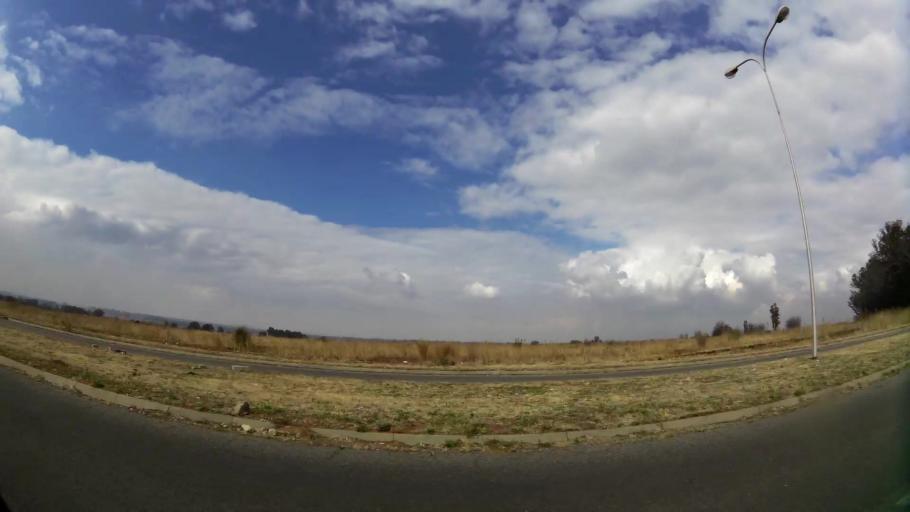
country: ZA
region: Gauteng
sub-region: Sedibeng District Municipality
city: Vanderbijlpark
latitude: -26.7275
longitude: 27.8743
